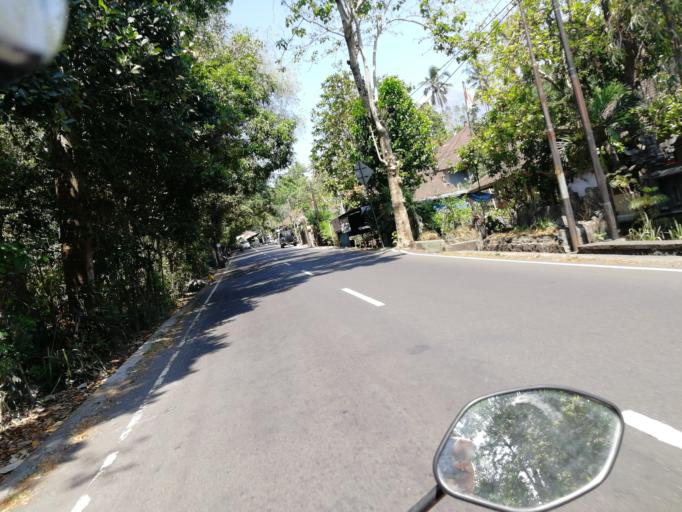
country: ID
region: Bali
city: Abang
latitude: -8.3908
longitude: 115.5997
